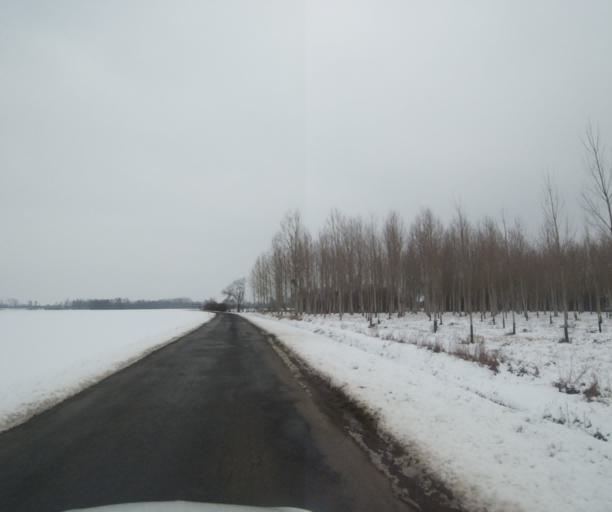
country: FR
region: Champagne-Ardenne
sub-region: Departement de la Haute-Marne
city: Saint-Dizier
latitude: 48.5716
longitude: 4.8908
